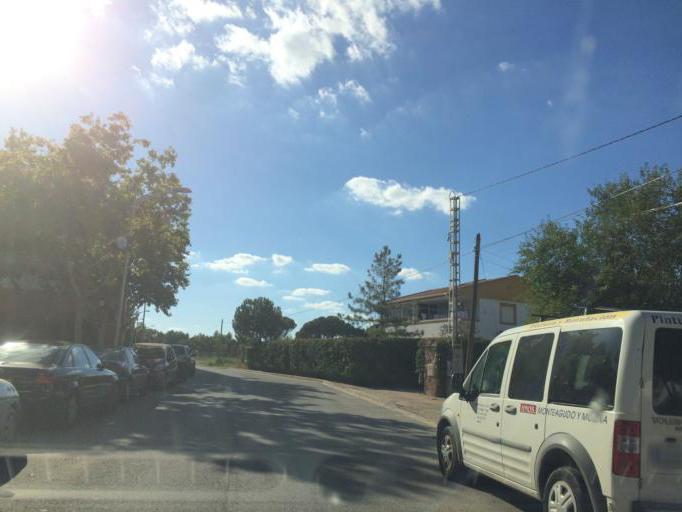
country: ES
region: Castille-La Mancha
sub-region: Provincia de Albacete
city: Albacete
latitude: 38.9942
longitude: -1.8775
